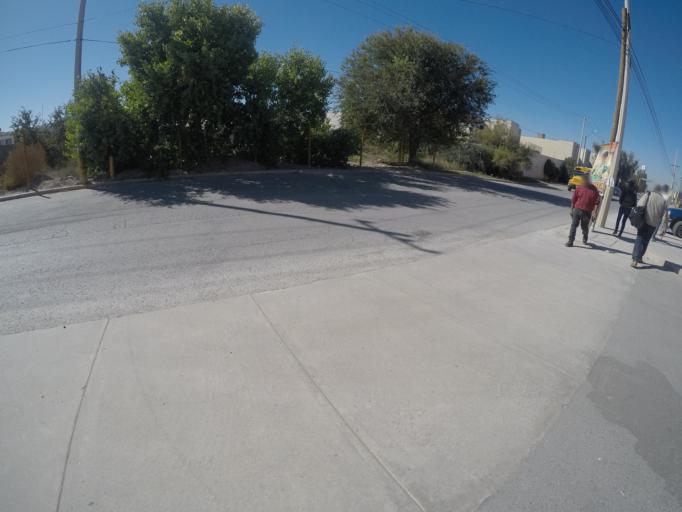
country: US
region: Texas
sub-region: El Paso County
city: Socorro
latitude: 31.6913
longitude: -106.3591
